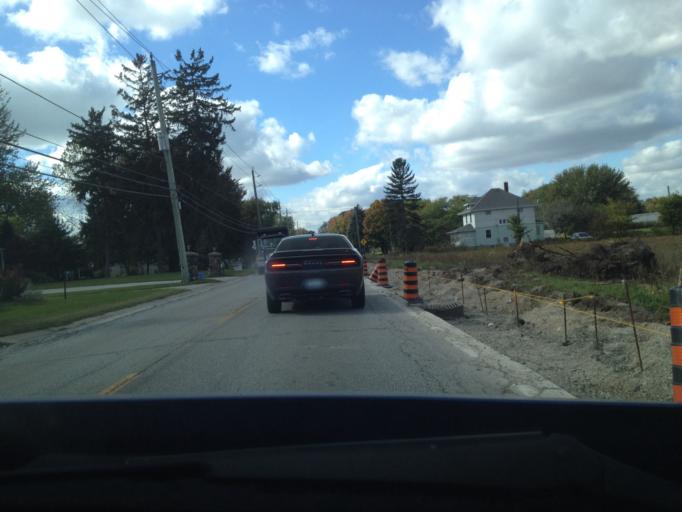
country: CA
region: Ontario
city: Amherstburg
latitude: 42.0342
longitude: -82.6090
